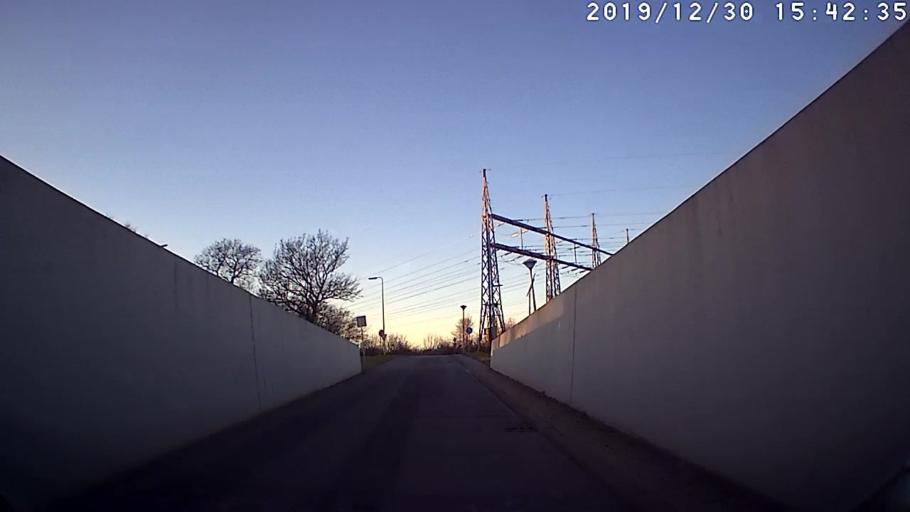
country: NL
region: Overijssel
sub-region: Gemeente Zwolle
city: Zwolle
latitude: 52.4699
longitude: 6.1327
